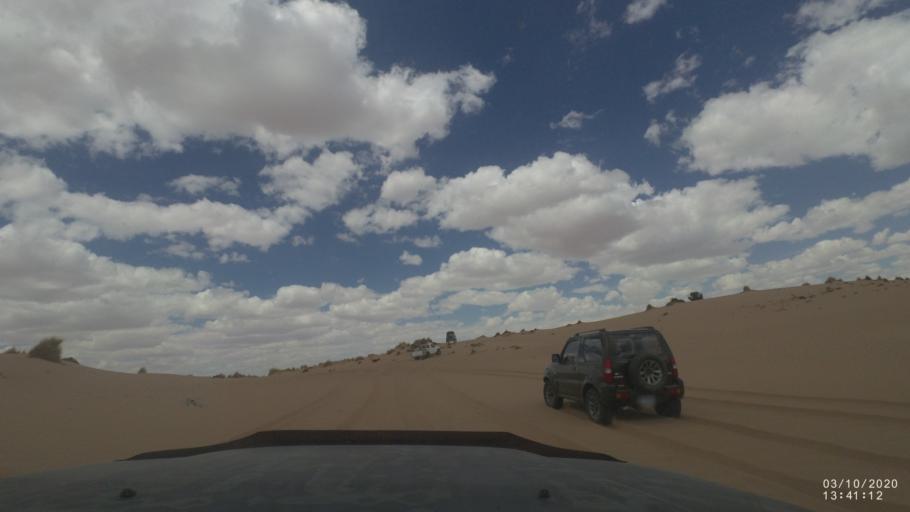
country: BO
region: Oruro
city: Poopo
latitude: -18.6915
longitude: -67.5302
